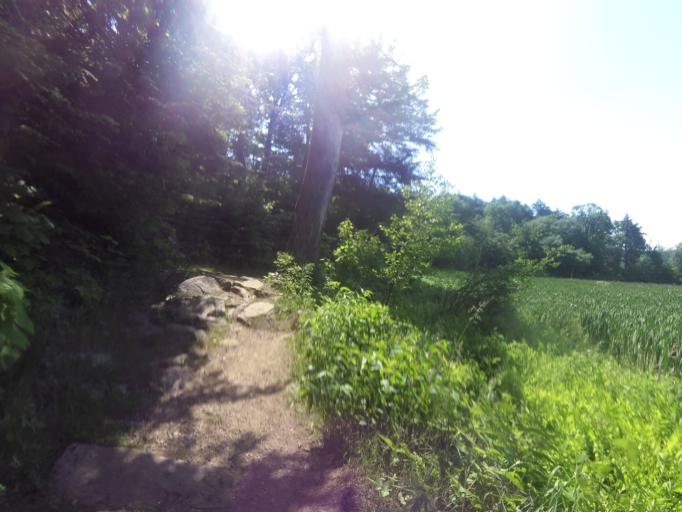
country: CA
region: Quebec
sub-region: Outaouais
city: Wakefield
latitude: 45.5393
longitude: -75.8773
